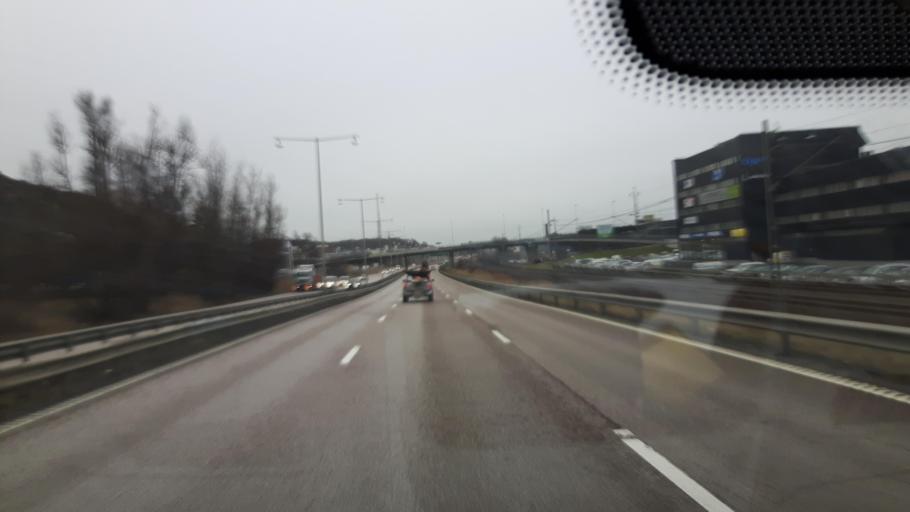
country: SE
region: Vaestra Goetaland
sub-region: Molndal
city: Moelndal
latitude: 57.6765
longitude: 12.0096
